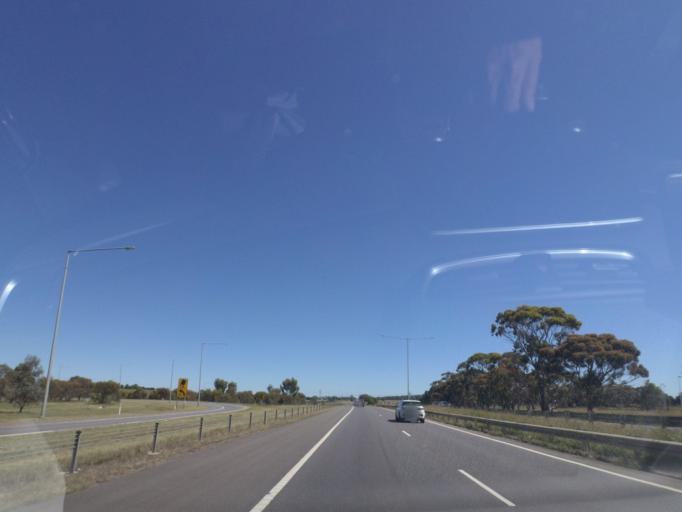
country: AU
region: Victoria
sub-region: Hume
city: Craigieburn
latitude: -37.5408
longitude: 144.9456
